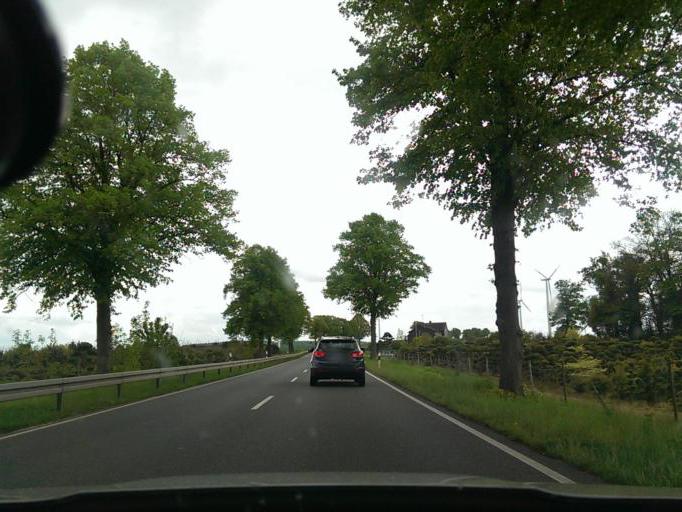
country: DE
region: Lower Saxony
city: Nordstemmen
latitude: 52.2047
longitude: 9.7474
